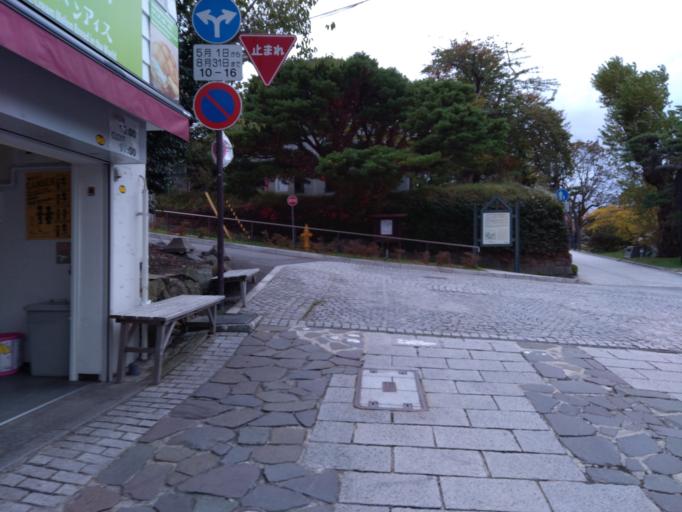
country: JP
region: Hokkaido
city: Hakodate
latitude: 41.7647
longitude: 140.7100
